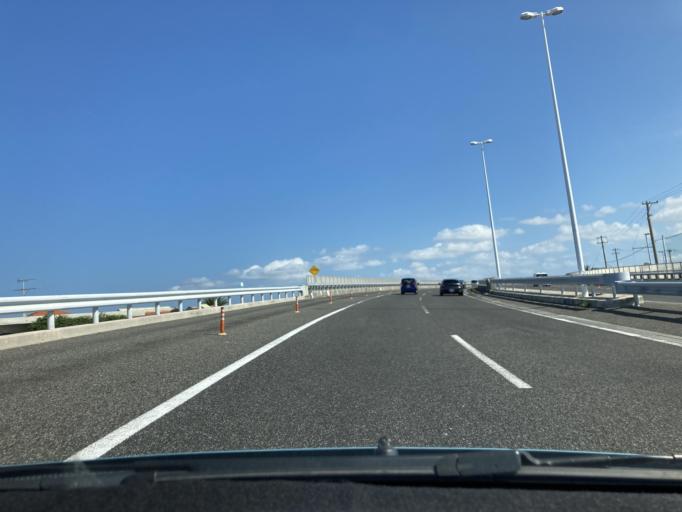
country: JP
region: Okinawa
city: Naha-shi
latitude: 26.2196
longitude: 127.6649
